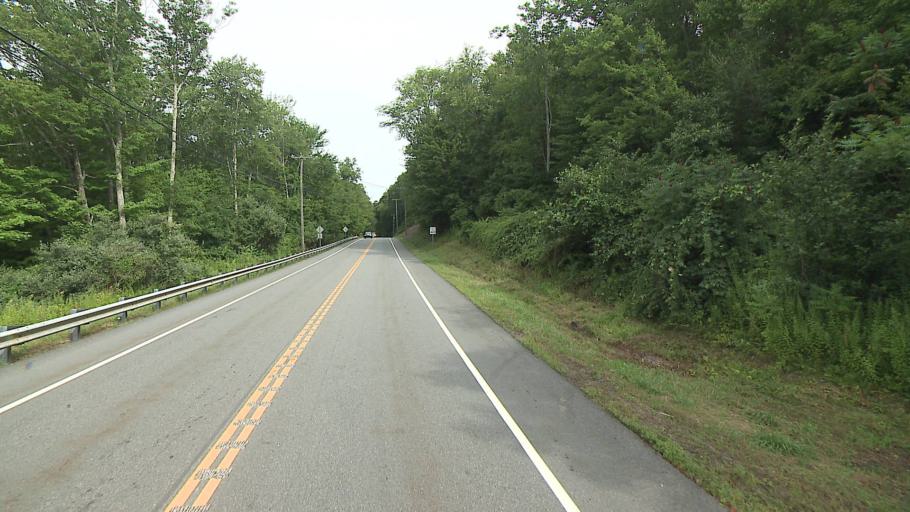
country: US
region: Connecticut
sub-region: Litchfield County
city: New Preston
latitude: 41.7097
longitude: -73.3052
